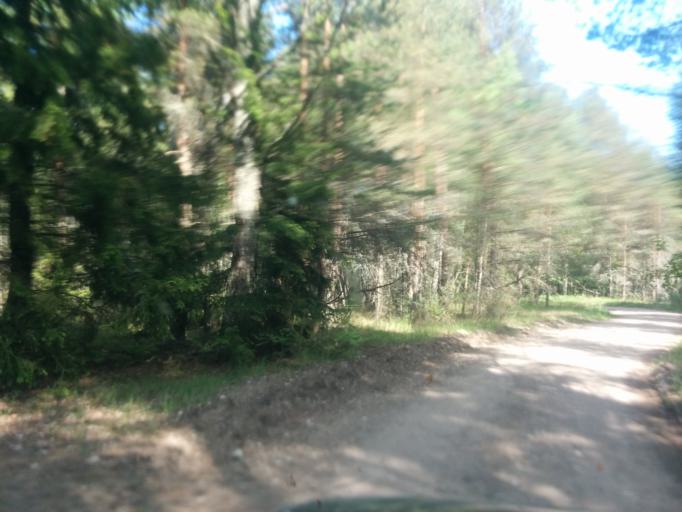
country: LV
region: Dundaga
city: Dundaga
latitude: 57.6227
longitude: 22.0993
